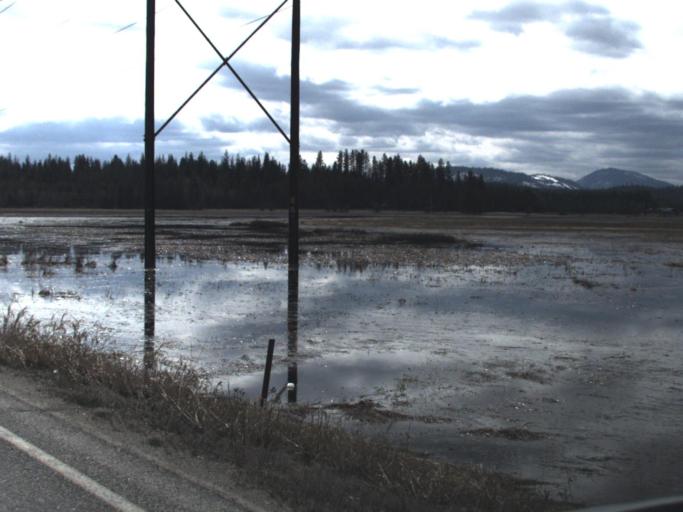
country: US
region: Washington
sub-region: Pend Oreille County
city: Newport
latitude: 48.2968
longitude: -117.2783
